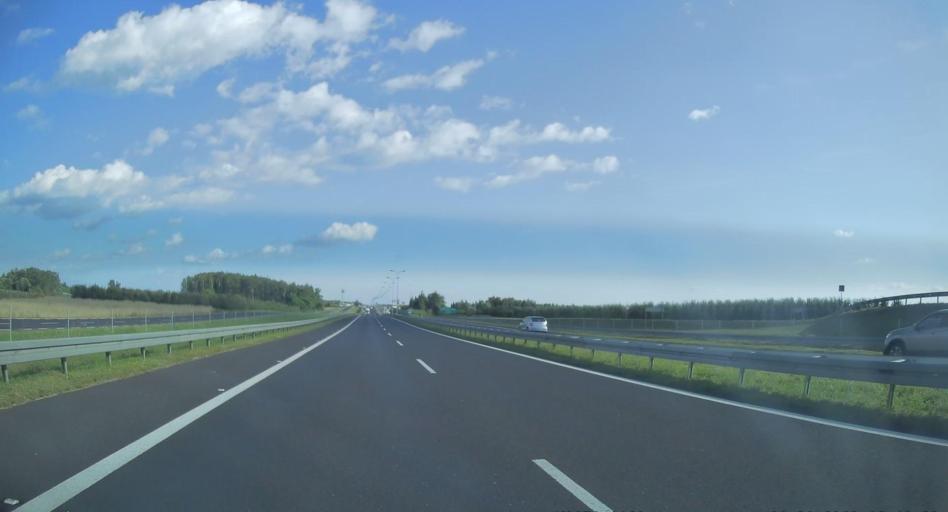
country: PL
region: Masovian Voivodeship
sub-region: Powiat grojecki
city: Goszczyn
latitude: 51.7528
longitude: 20.9075
